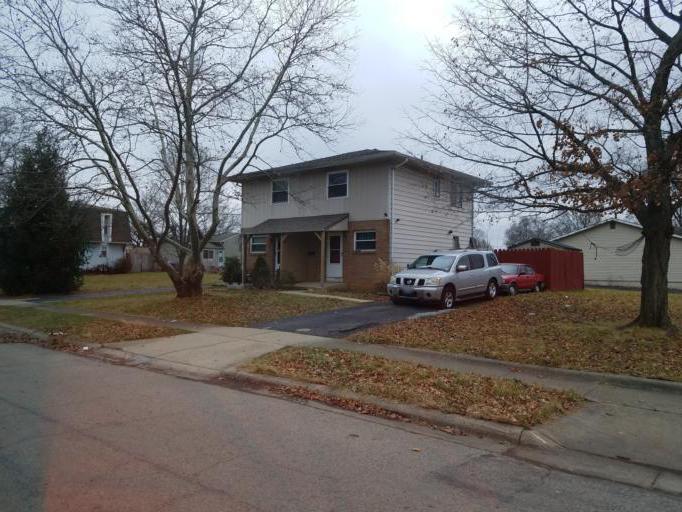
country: US
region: Ohio
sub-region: Franklin County
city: Minerva Park
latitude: 40.0836
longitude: -82.9654
